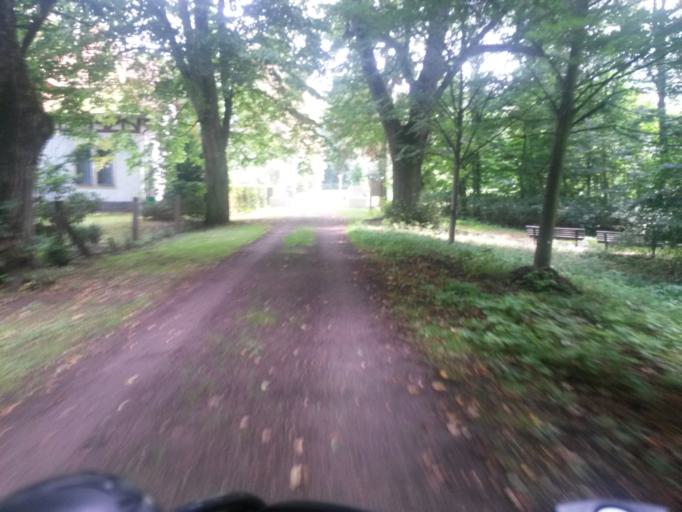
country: DE
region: Brandenburg
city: Angermunde
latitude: 53.0605
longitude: 13.9638
